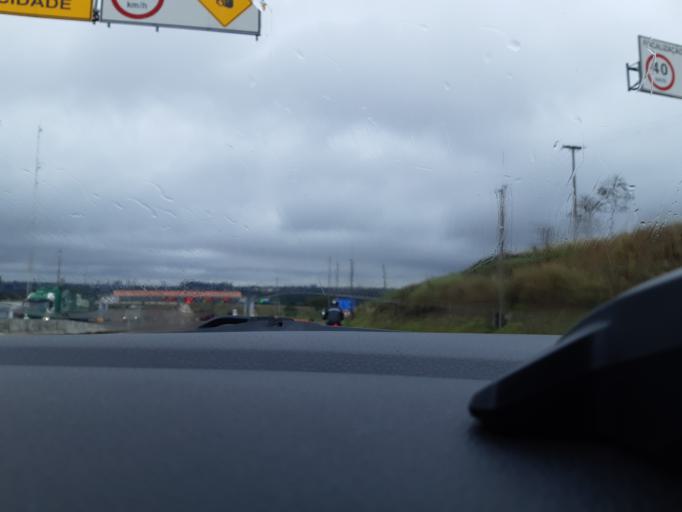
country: BR
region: Sao Paulo
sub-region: Ourinhos
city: Ourinhos
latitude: -23.0046
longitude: -49.9114
